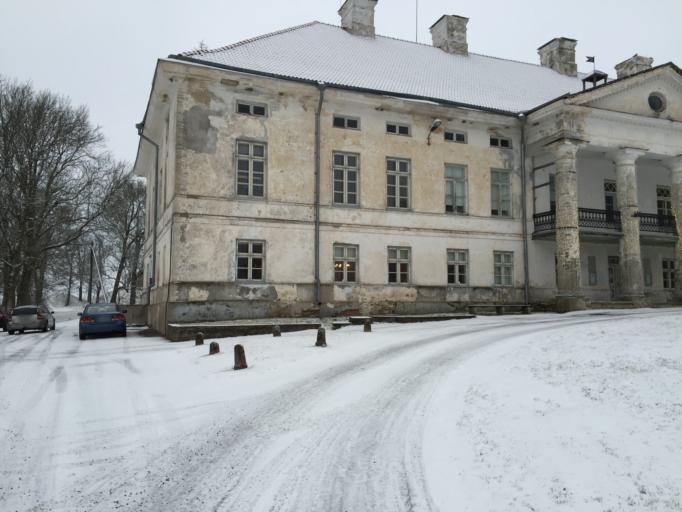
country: EE
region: Laeaene
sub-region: Lihula vald
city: Lihula
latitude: 58.6930
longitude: 23.8383
